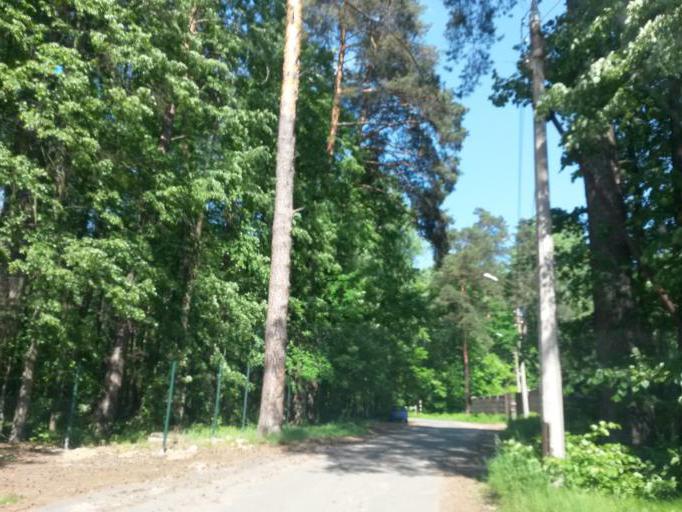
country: RU
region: Moskovskaya
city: Danki
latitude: 54.9112
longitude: 37.5717
